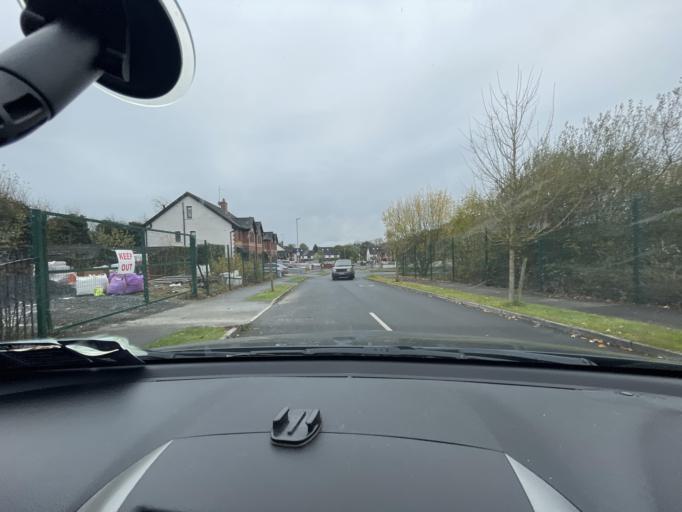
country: IE
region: Ulster
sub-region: An Cabhan
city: Virginia
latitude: 53.8386
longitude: -7.0804
